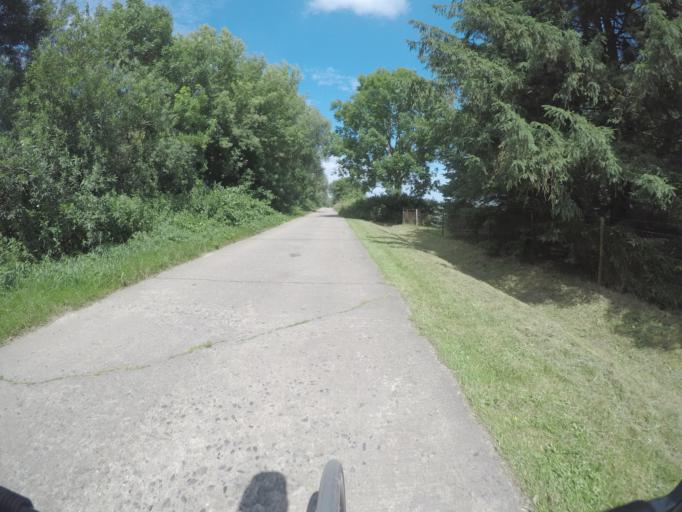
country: DE
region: Mecklenburg-Vorpommern
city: Altefahr
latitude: 54.3340
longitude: 13.1286
